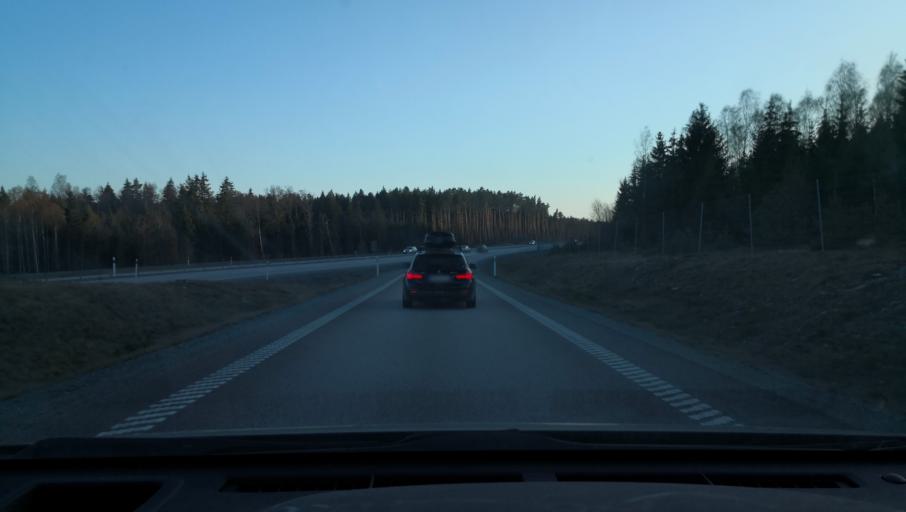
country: SE
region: Uppsala
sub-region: Enkopings Kommun
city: Hummelsta
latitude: 59.6275
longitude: 16.8332
